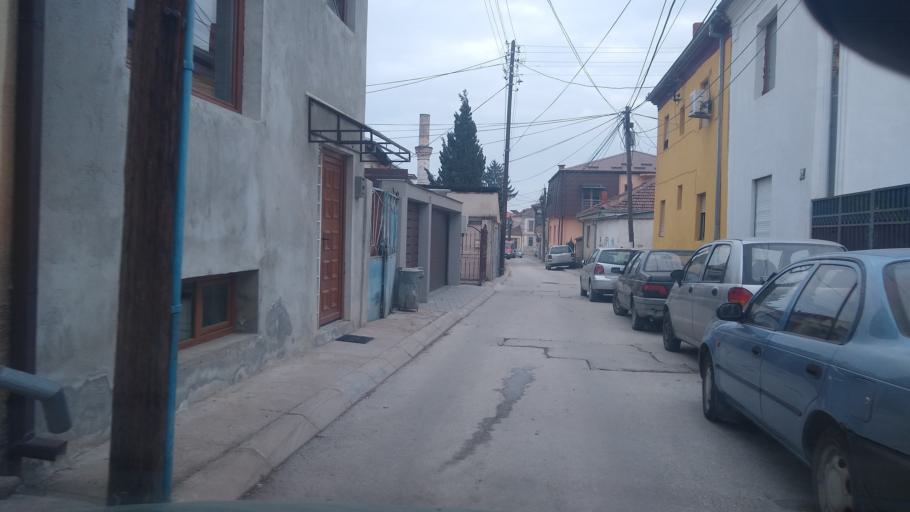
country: MK
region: Bitola
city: Bitola
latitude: 41.0289
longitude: 21.3288
